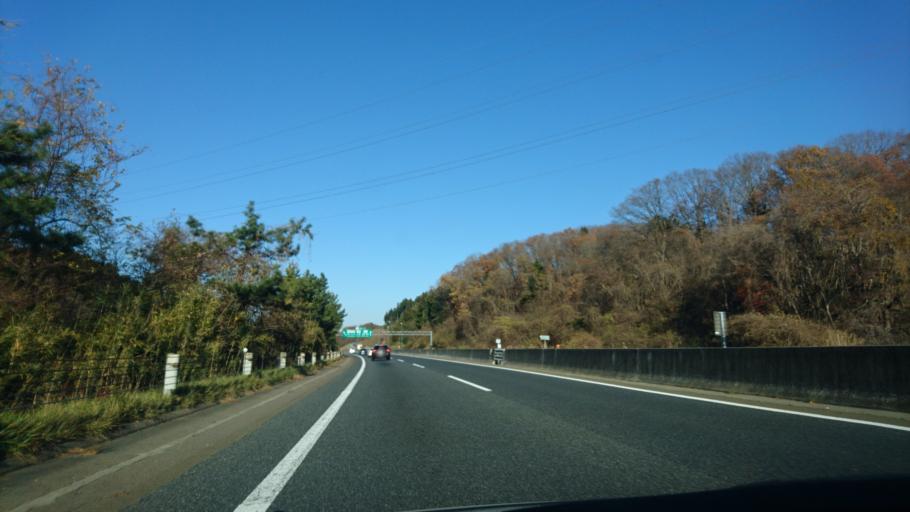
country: JP
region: Miyagi
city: Tomiya
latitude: 38.3675
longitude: 140.8848
